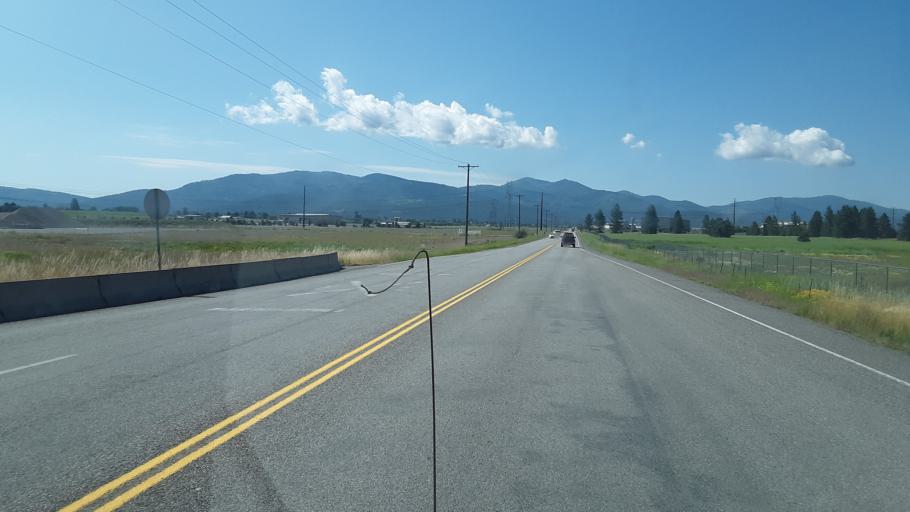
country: US
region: Idaho
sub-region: Kootenai County
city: Post Falls
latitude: 47.7517
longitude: -117.0021
